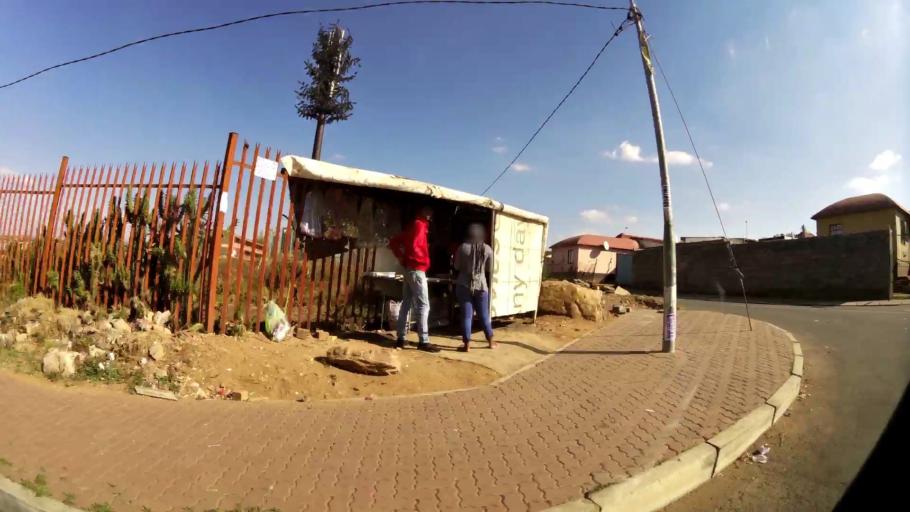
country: ZA
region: Gauteng
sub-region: City of Johannesburg Metropolitan Municipality
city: Soweto
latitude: -26.2281
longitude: 27.9192
